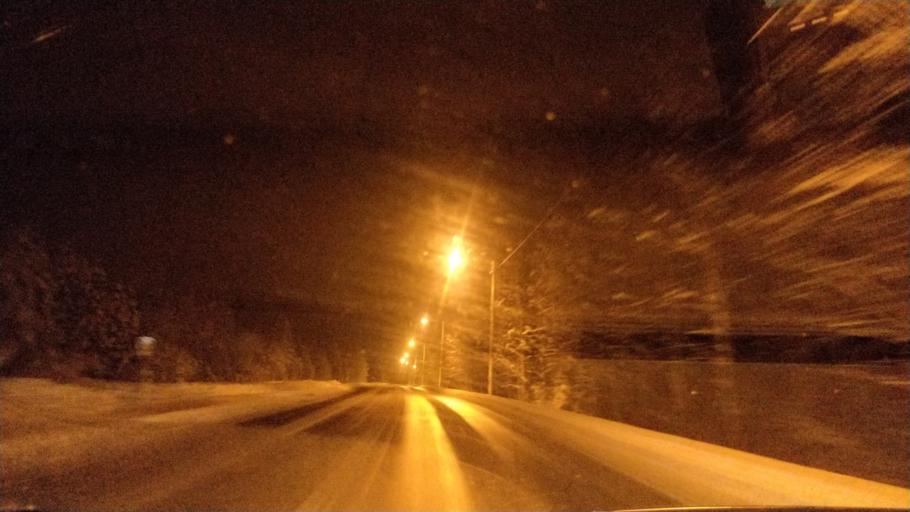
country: FI
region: Lapland
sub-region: Rovaniemi
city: Rovaniemi
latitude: 66.4017
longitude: 25.3892
